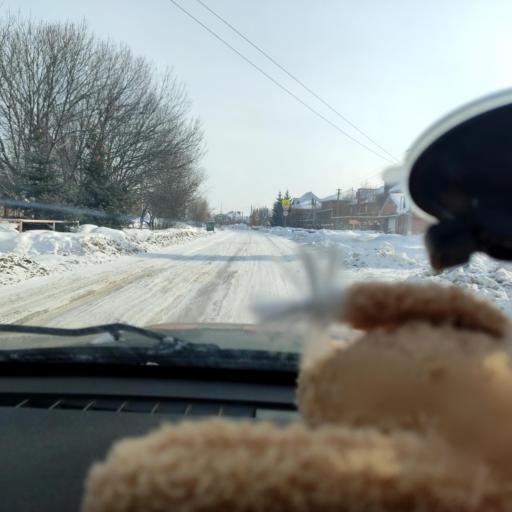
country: RU
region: Samara
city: Podstepki
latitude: 53.5103
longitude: 49.1302
